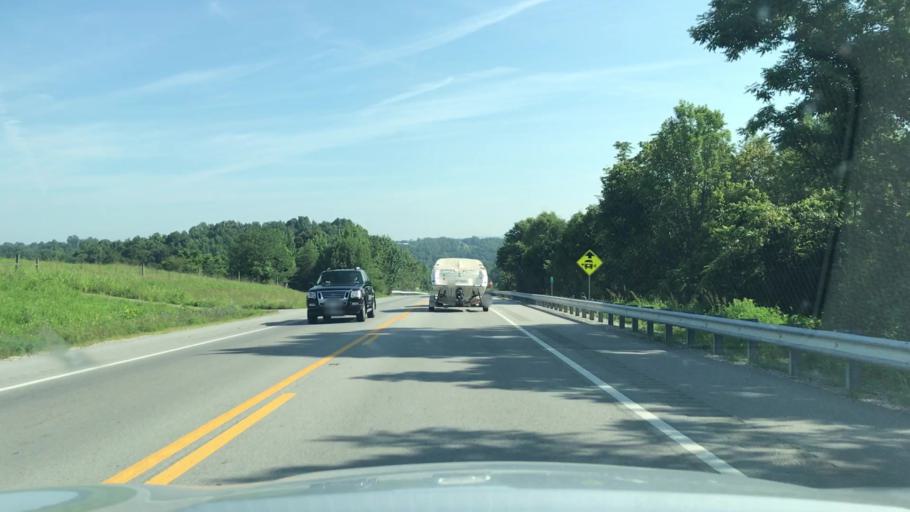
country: US
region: Tennessee
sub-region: Pickett County
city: Byrdstown
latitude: 36.5918
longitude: -85.1243
